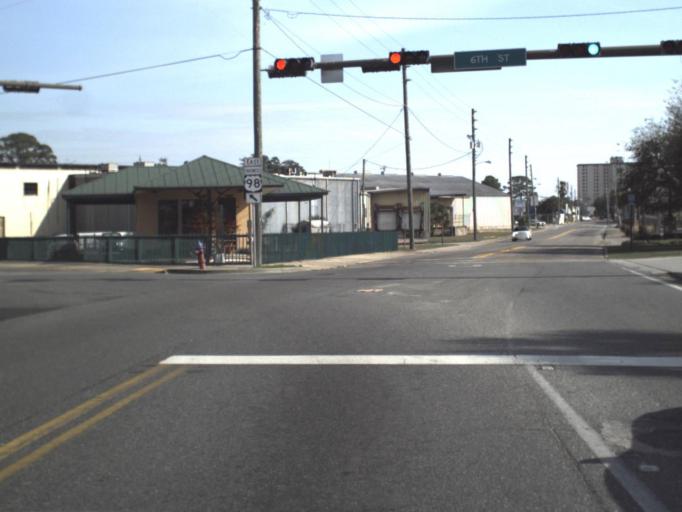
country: US
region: Florida
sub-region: Bay County
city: Panama City
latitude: 30.1590
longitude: -85.6665
